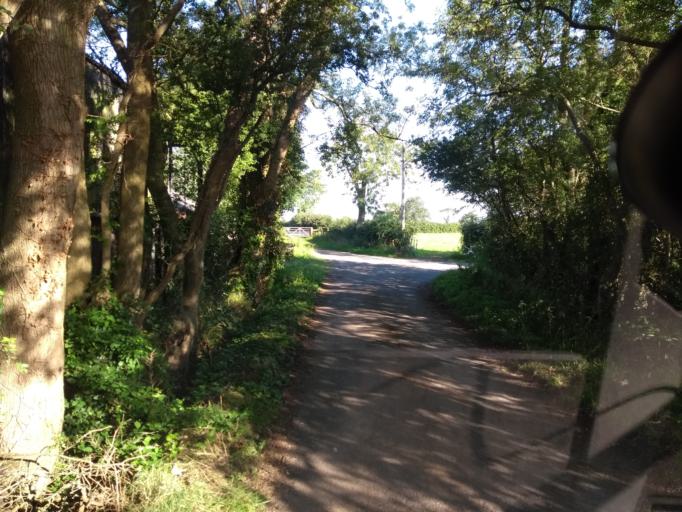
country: GB
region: England
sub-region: Somerset
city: Axbridge
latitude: 51.2620
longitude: -2.8460
